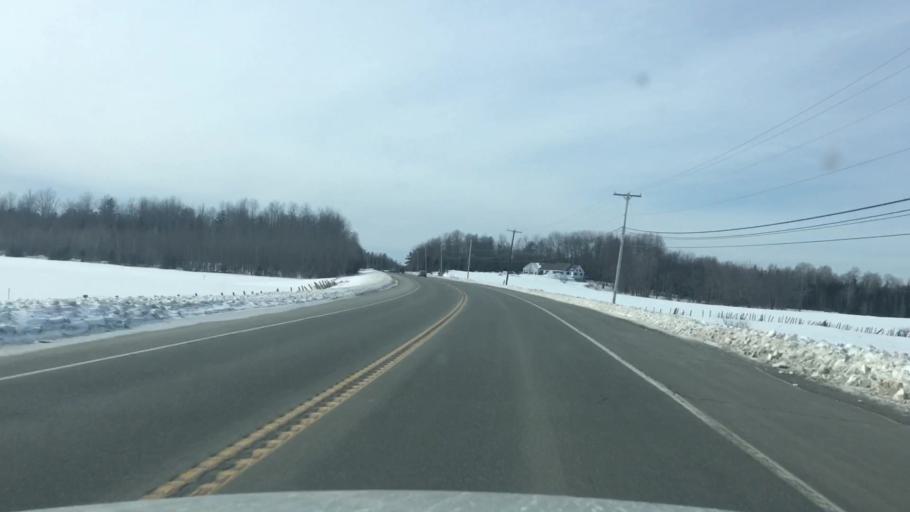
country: US
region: Maine
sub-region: Penobscot County
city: Kenduskeag
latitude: 44.9109
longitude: -68.8994
